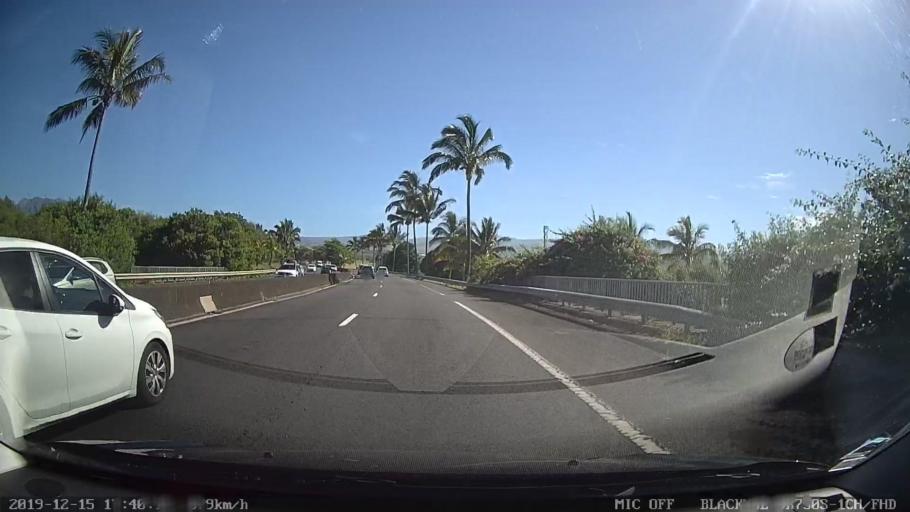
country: RE
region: Reunion
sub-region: Reunion
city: Saint-Pierre
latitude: -21.3219
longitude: 55.4880
